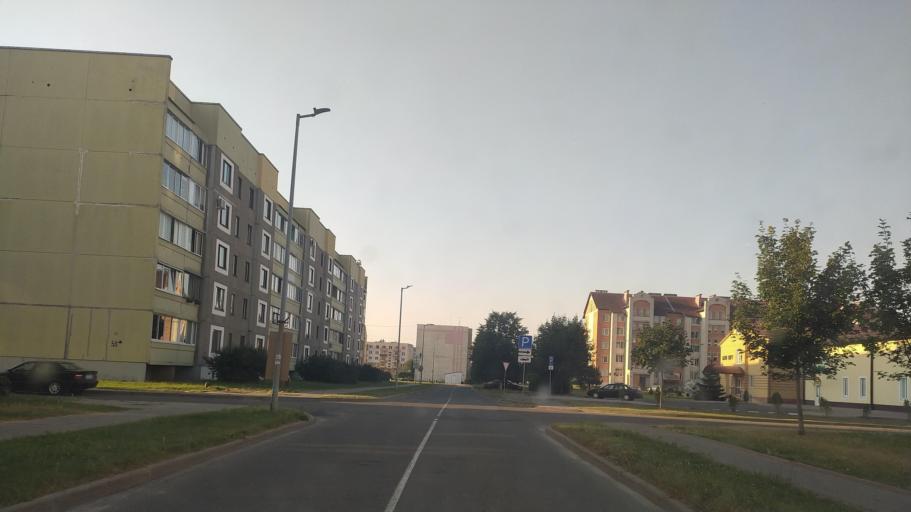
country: BY
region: Brest
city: Byaroza
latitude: 52.5454
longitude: 24.9844
